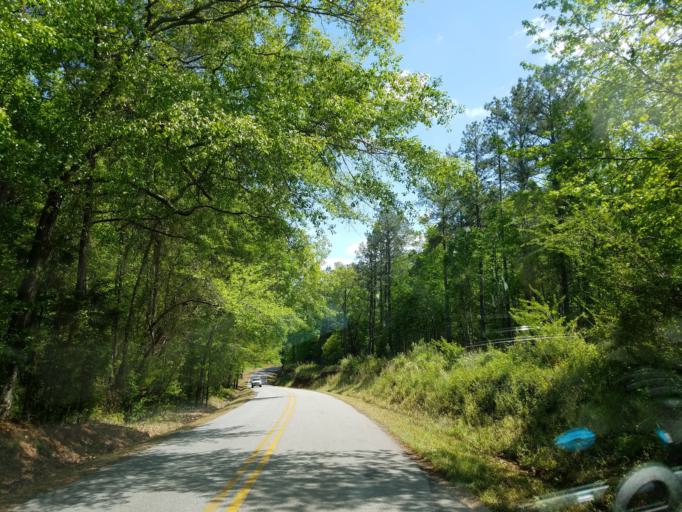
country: US
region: Georgia
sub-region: Monroe County
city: Forsyth
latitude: 33.1324
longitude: -83.9743
